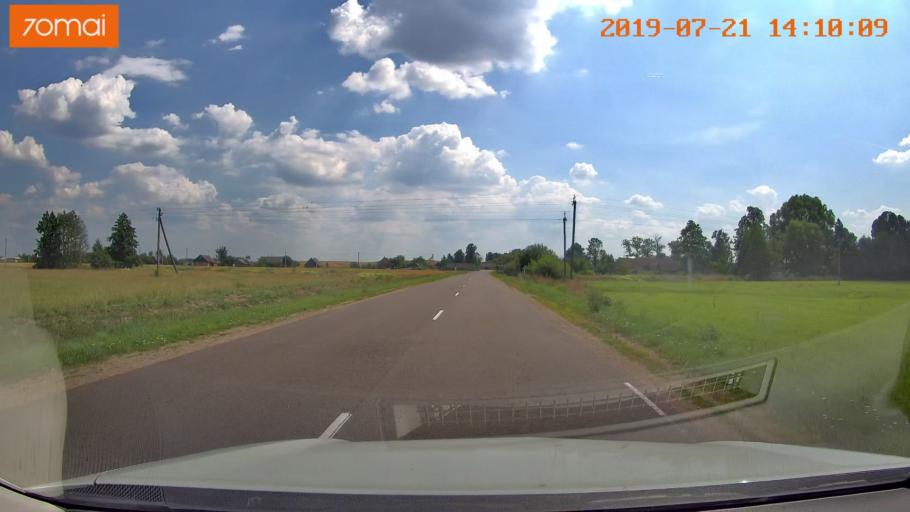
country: BY
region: Grodnenskaya
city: Karelichy
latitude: 53.6657
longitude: 26.1340
